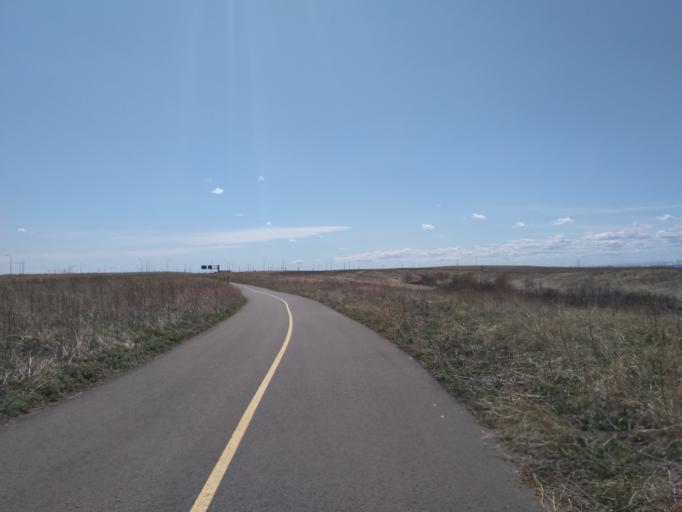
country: CA
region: Alberta
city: Chestermere
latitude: 51.0214
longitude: -113.9245
